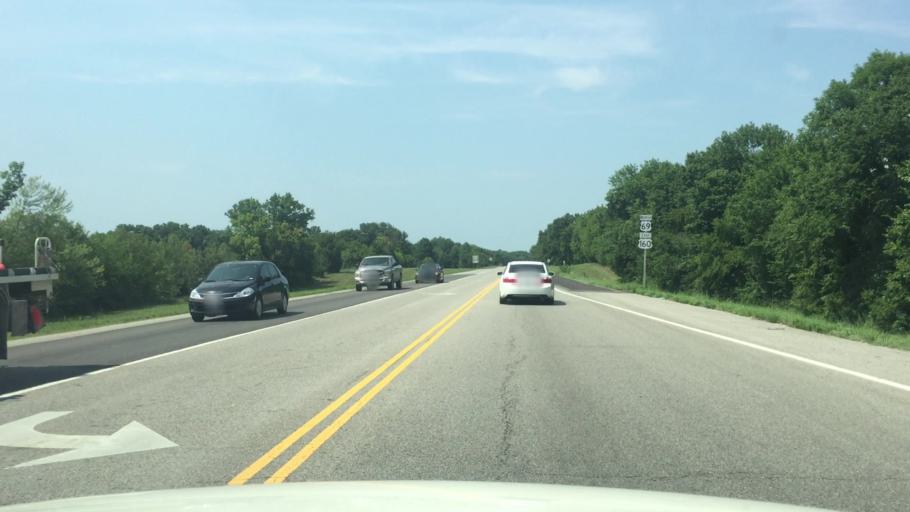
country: US
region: Kansas
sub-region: Crawford County
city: Pittsburg
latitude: 37.3969
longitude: -94.7192
